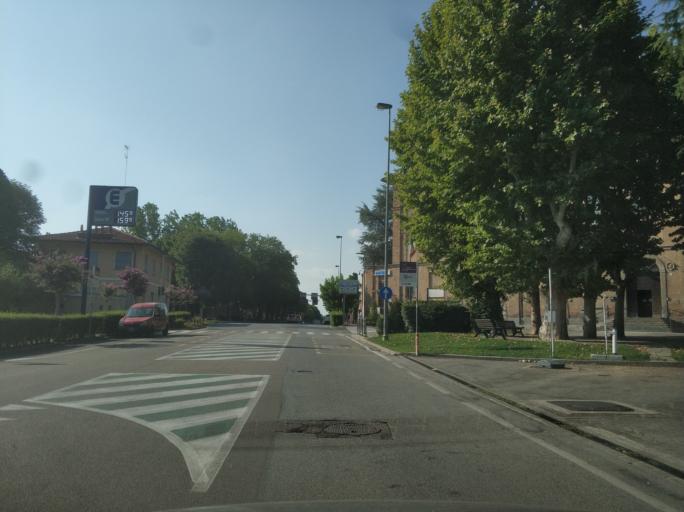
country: IT
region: Piedmont
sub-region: Provincia di Cuneo
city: Bra
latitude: 44.7015
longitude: 7.8479
